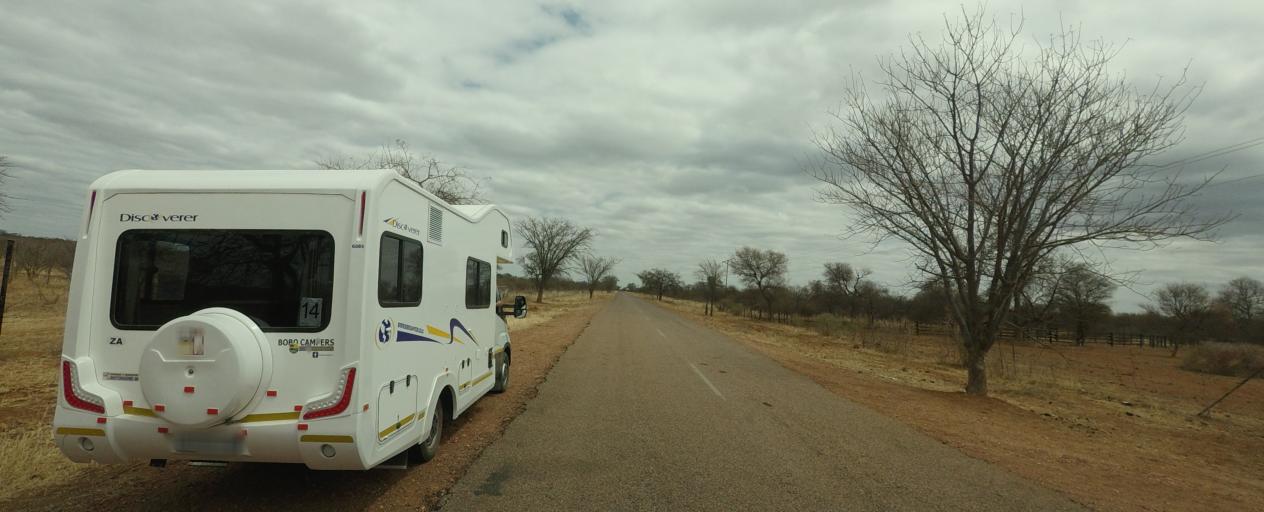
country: BW
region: Central
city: Makobeng
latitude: -22.9378
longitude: 28.1641
